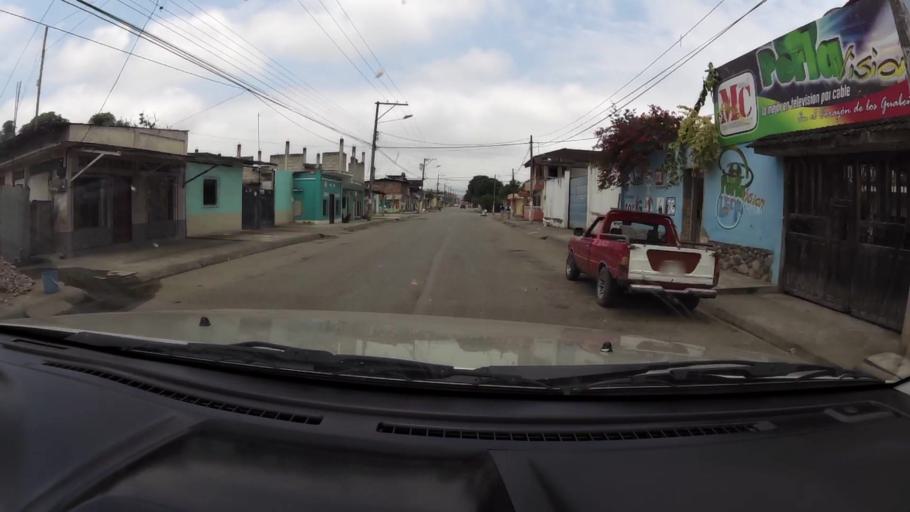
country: EC
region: El Oro
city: Pasaje
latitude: -3.2413
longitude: -79.8277
